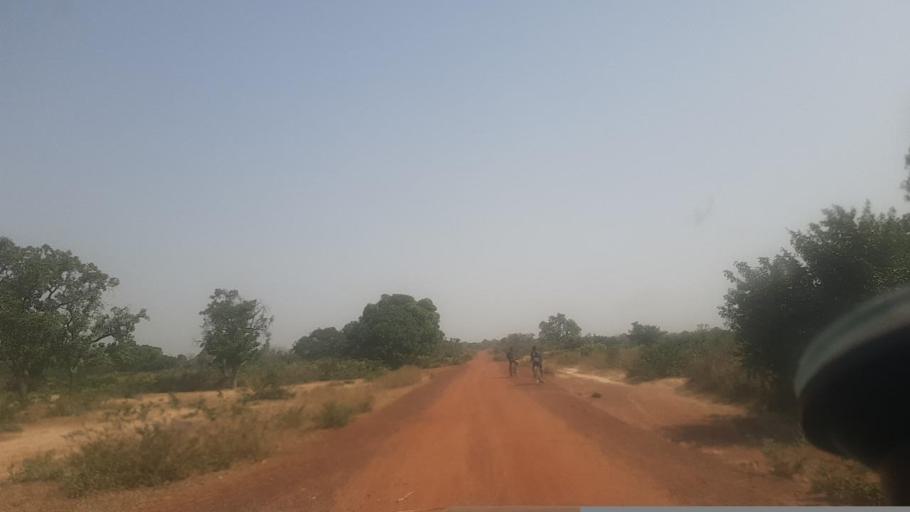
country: ML
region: Segou
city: Segou
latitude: 12.9317
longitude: -6.2856
